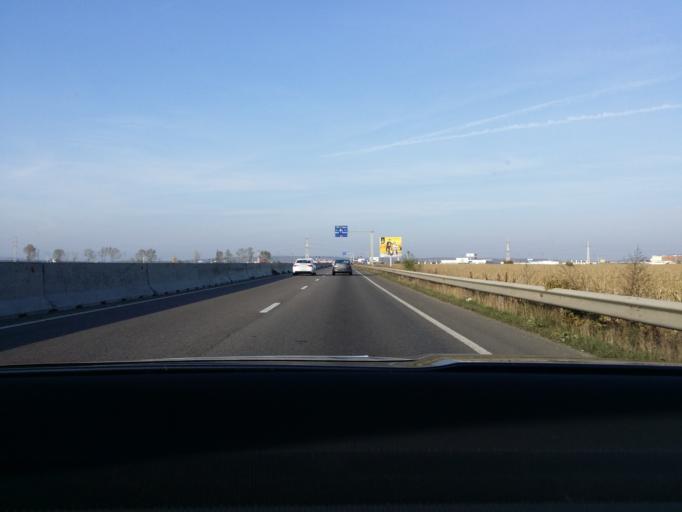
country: RO
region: Prahova
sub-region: Comuna Targsoru Vechi
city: Strejnicu
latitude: 44.9538
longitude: 25.9631
